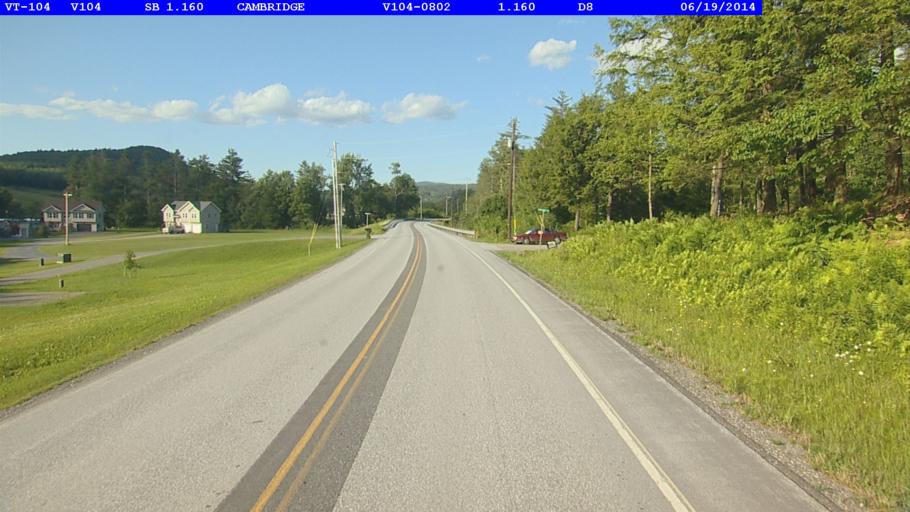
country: US
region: Vermont
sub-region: Chittenden County
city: Jericho
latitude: 44.6425
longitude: -72.9102
